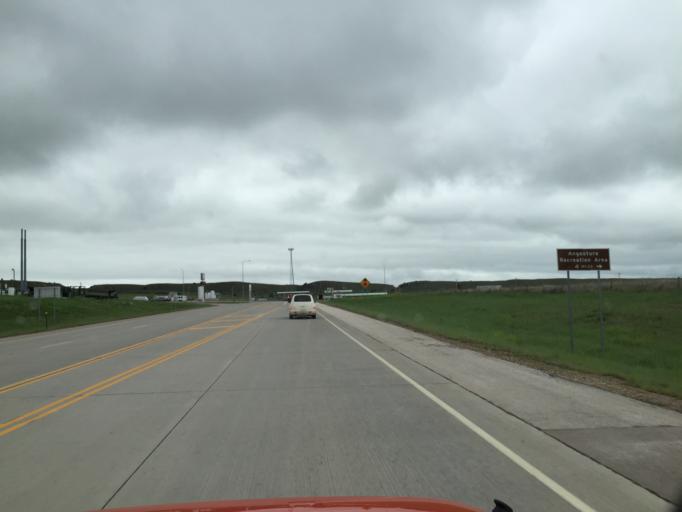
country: US
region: South Dakota
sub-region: Fall River County
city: Hot Springs
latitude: 43.4004
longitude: -103.4002
